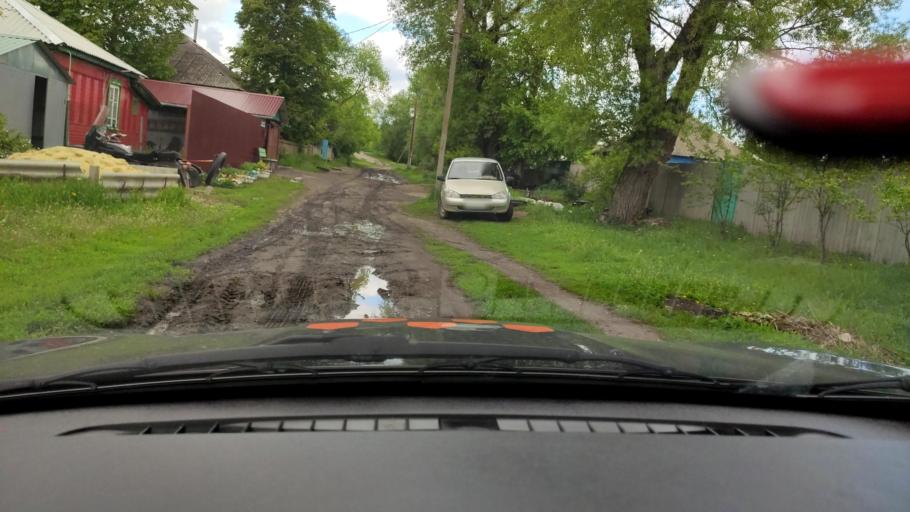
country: RU
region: Voronezj
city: Uryv-Pokrovka
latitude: 51.1057
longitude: 39.1564
